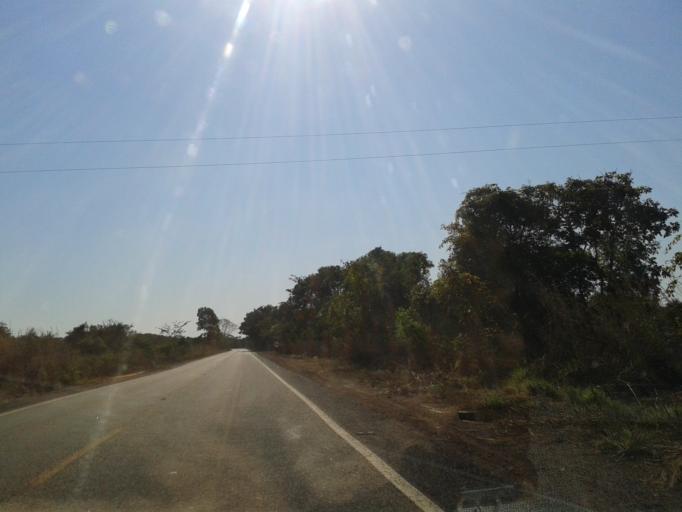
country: BR
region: Goias
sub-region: Mozarlandia
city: Mozarlandia
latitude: -14.6547
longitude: -50.5246
